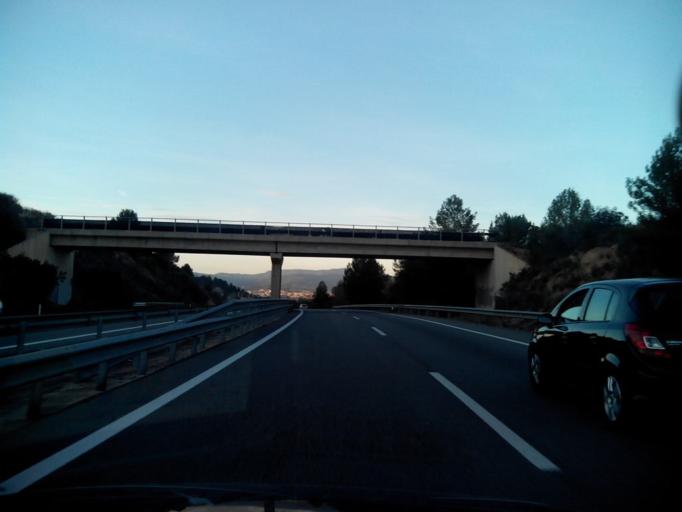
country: ES
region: Catalonia
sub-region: Provincia de Barcelona
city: Terrassa
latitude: 41.5304
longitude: 2.0228
